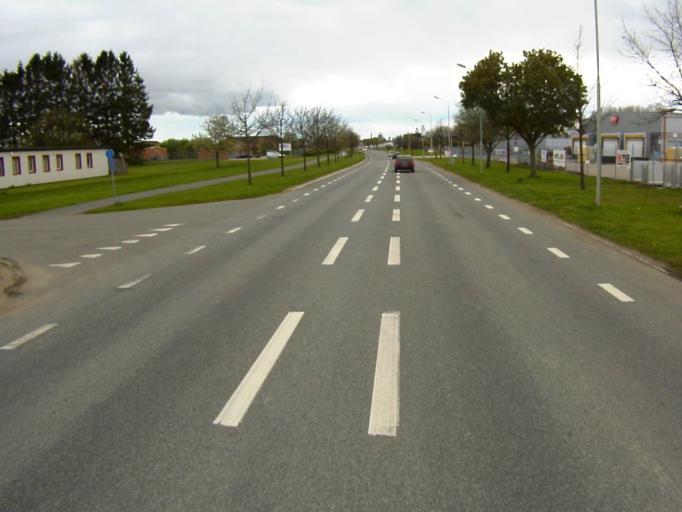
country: SE
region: Skane
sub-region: Kristianstads Kommun
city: Kristianstad
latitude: 56.0552
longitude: 14.1674
